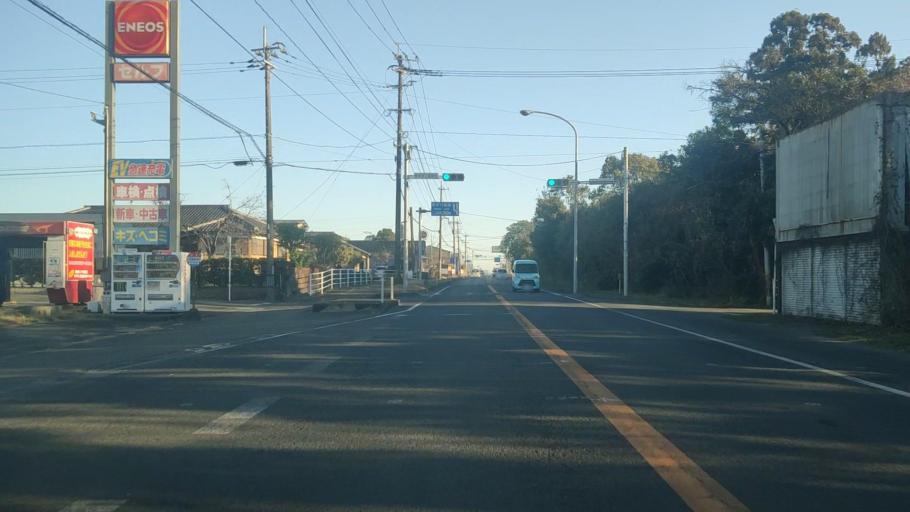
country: JP
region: Miyazaki
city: Takanabe
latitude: 32.2190
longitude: 131.5405
